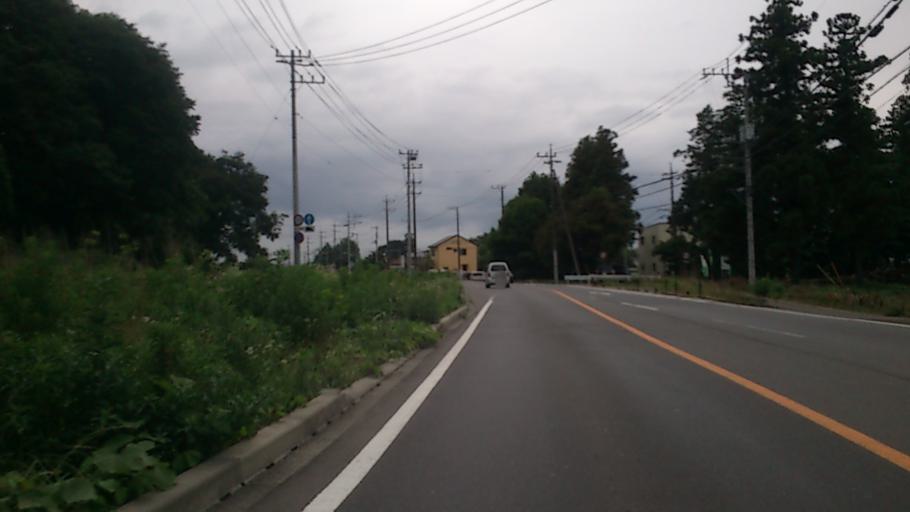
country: JP
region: Ibaraki
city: Tsukuba
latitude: 36.1018
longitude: 140.0759
